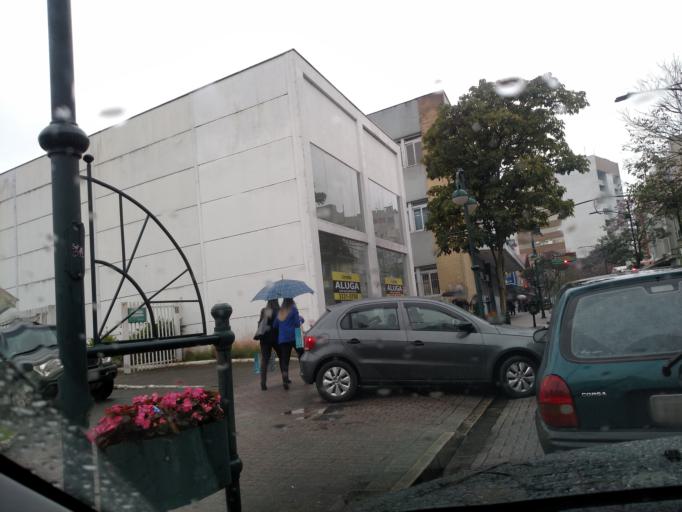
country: BR
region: Santa Catarina
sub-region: Blumenau
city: Blumenau
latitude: -26.9185
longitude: -49.0666
